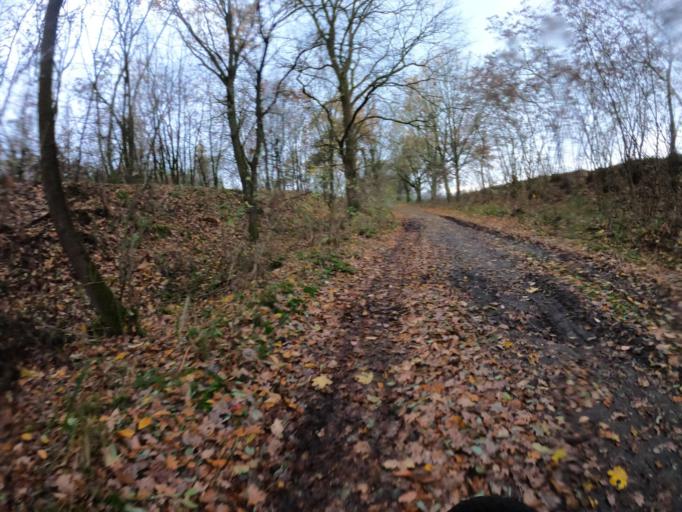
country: PL
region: West Pomeranian Voivodeship
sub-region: Powiat walecki
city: Tuczno
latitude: 53.2135
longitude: 16.2351
